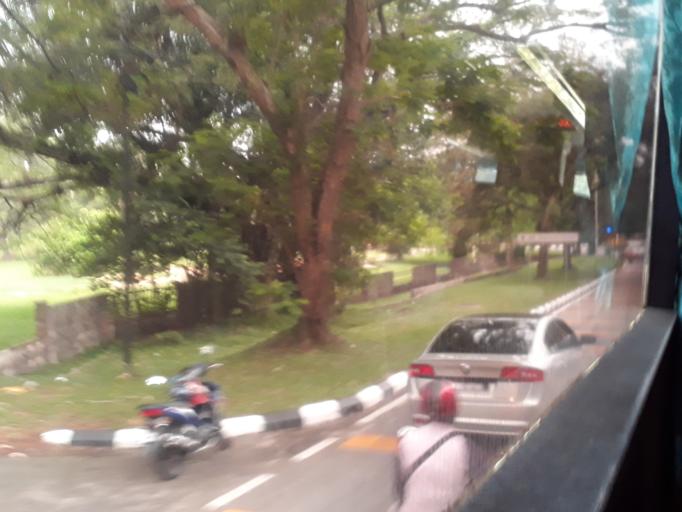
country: MY
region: Perak
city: Ipoh
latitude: 4.5979
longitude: 101.1063
